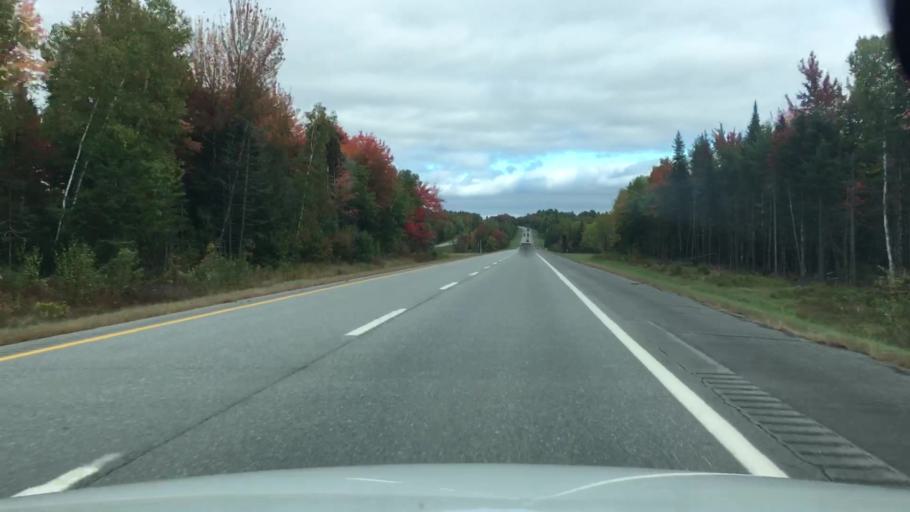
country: US
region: Maine
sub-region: Penobscot County
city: Carmel
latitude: 44.7764
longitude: -69.0505
